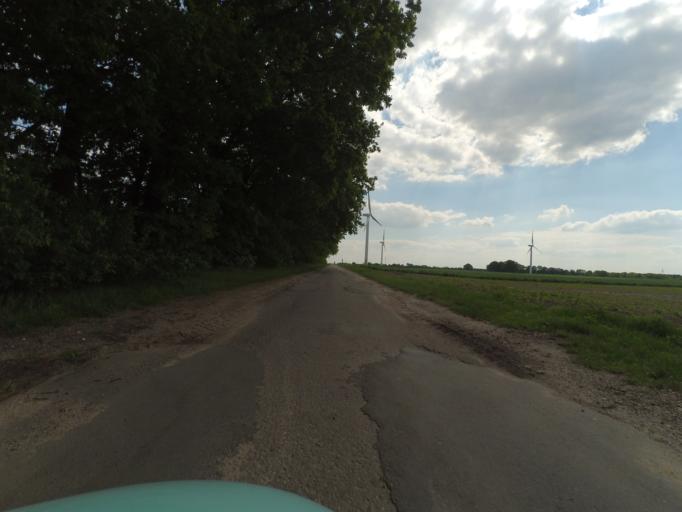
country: DE
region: Lower Saxony
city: Uetze
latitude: 52.4544
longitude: 10.1709
